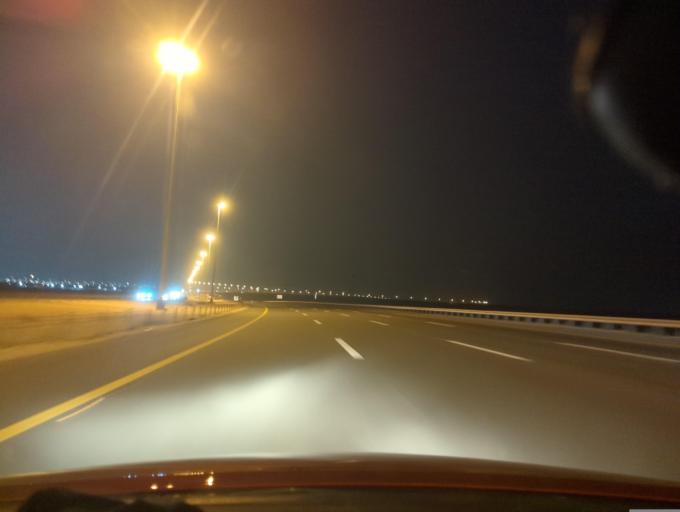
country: AE
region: Abu Dhabi
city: Abu Dhabi
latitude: 24.4339
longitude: 54.7646
